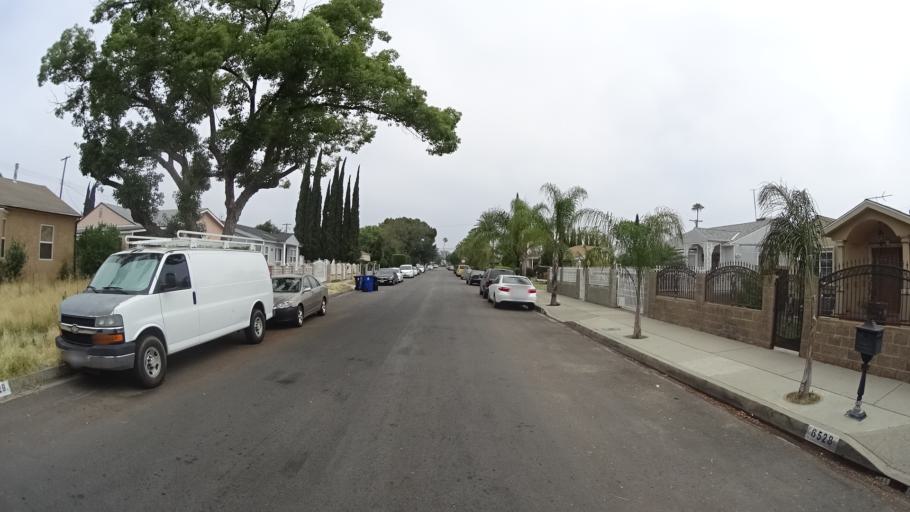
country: US
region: California
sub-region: Los Angeles County
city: North Hollywood
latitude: 34.1892
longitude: -118.4081
